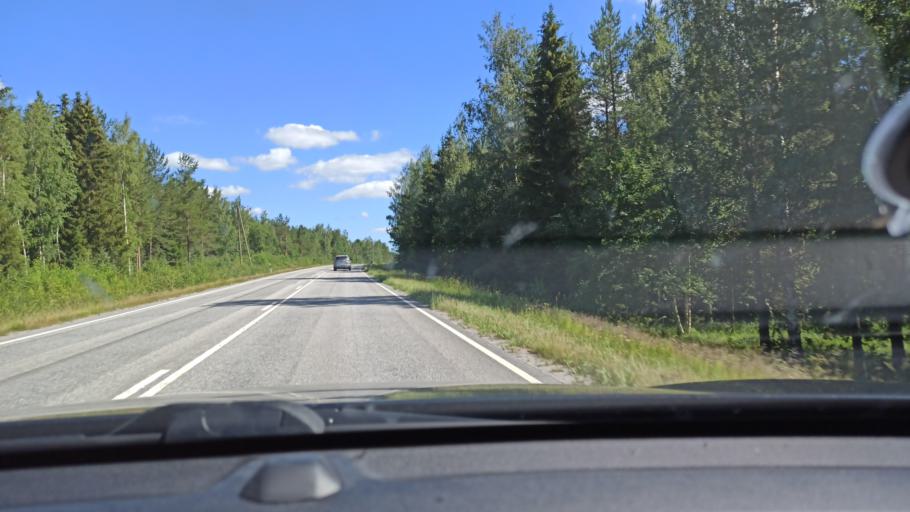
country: FI
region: Ostrobothnia
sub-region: Vaasa
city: Malax
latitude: 62.9710
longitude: 21.5930
